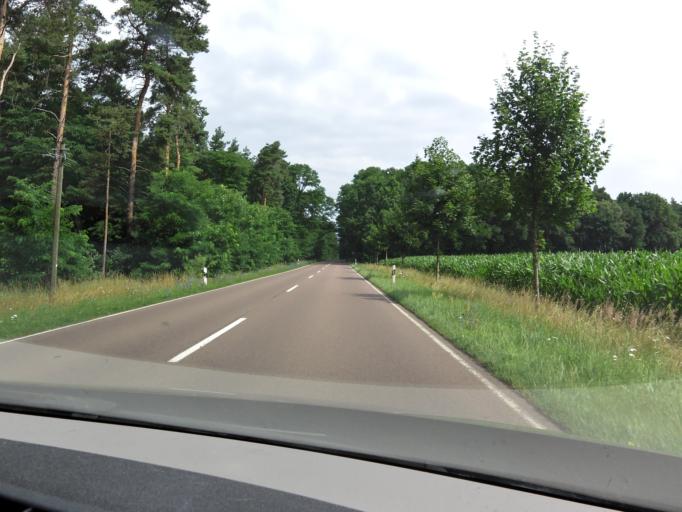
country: DE
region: Saxony-Anhalt
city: Kemberg
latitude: 51.7516
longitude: 12.6308
